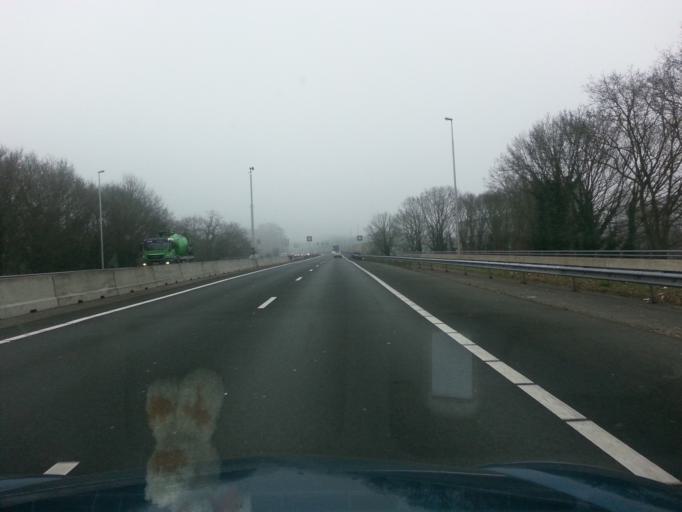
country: NL
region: Gelderland
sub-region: Gemeente Ede
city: Bennekom
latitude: 52.0127
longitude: 5.6715
